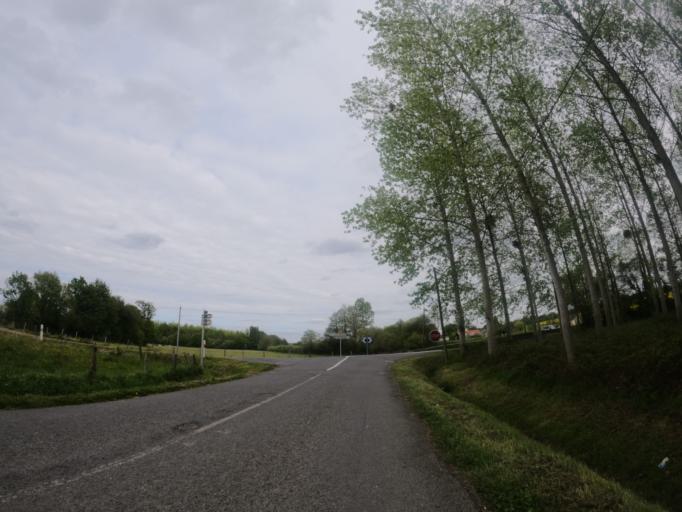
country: FR
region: Pays de la Loire
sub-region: Departement de la Loire-Atlantique
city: Rouge
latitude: 47.7379
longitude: -1.4286
